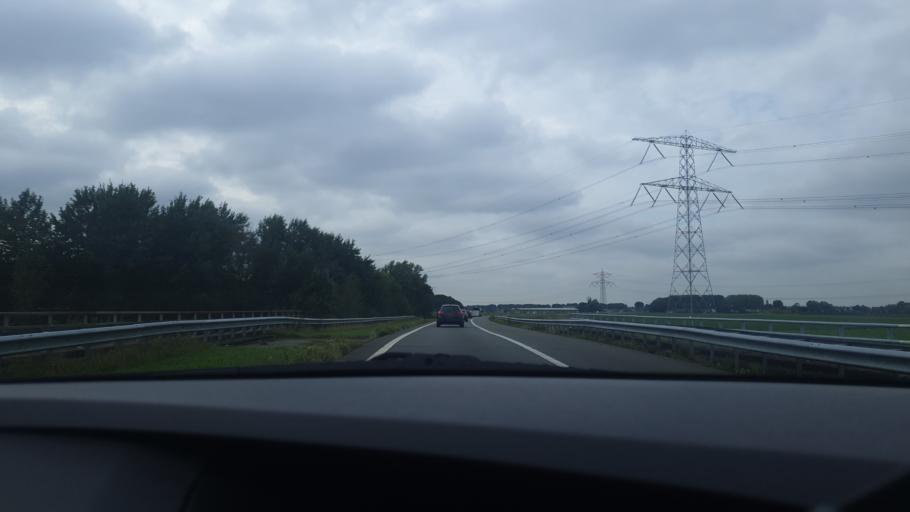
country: NL
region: North Brabant
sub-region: Gemeente Moerdijk
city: Klundert
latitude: 51.6367
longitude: 4.5426
